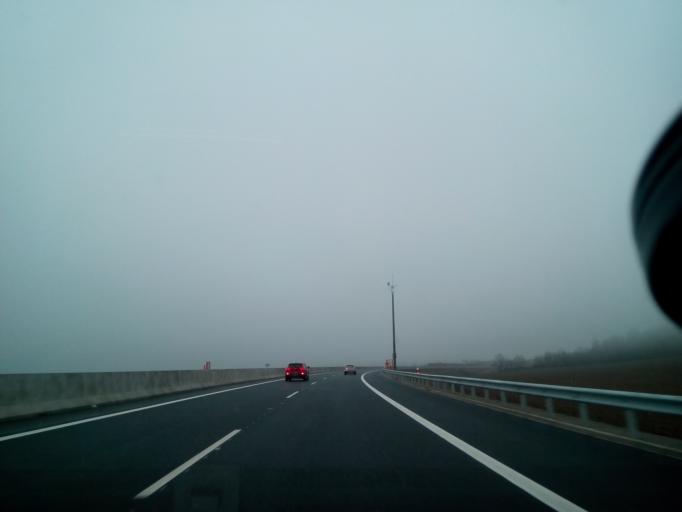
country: SK
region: Presovsky
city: Sabinov
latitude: 49.0078
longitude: 21.0513
